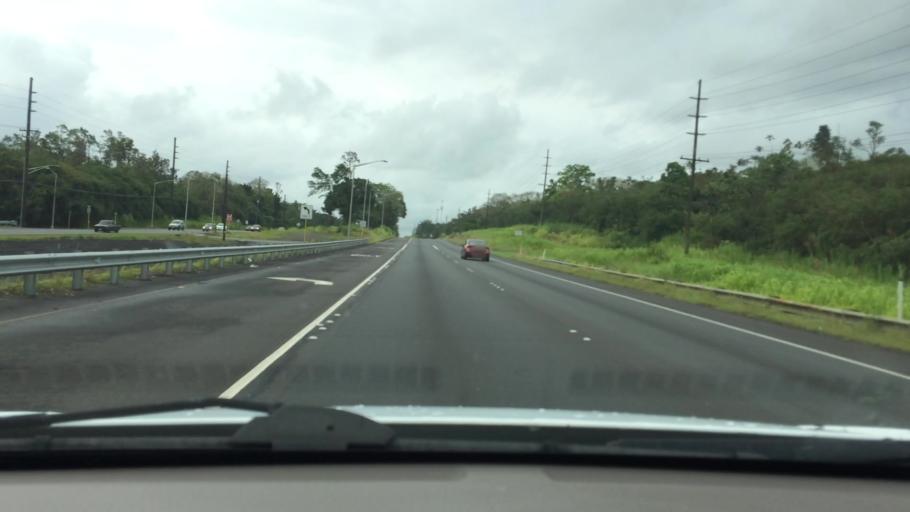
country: US
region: Hawaii
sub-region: Hawaii County
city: Kea'au
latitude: 19.6515
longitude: -155.0526
